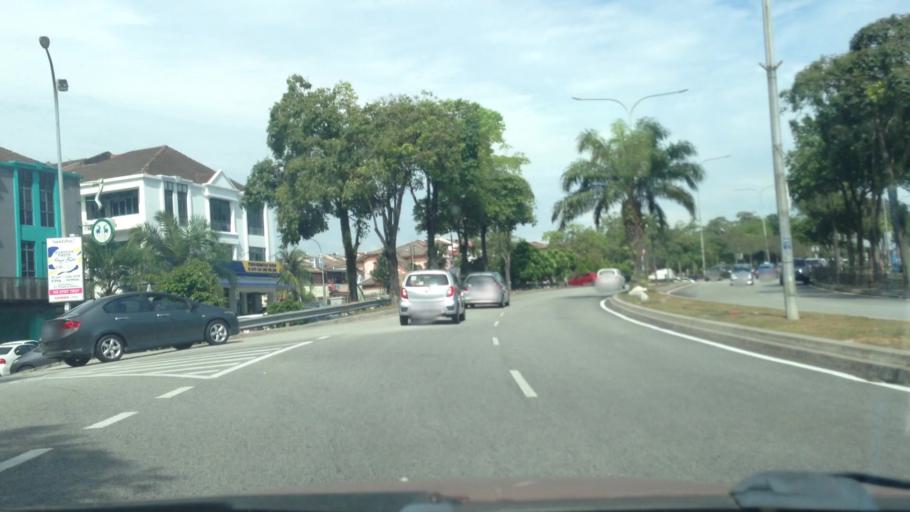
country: MY
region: Selangor
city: Subang Jaya
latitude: 3.0471
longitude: 101.5864
